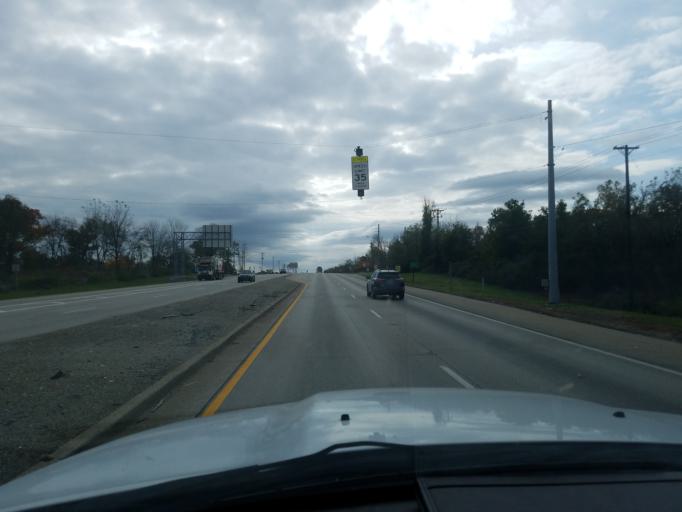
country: US
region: Kentucky
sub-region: Jefferson County
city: Fern Creek
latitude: 38.1392
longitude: -85.5822
